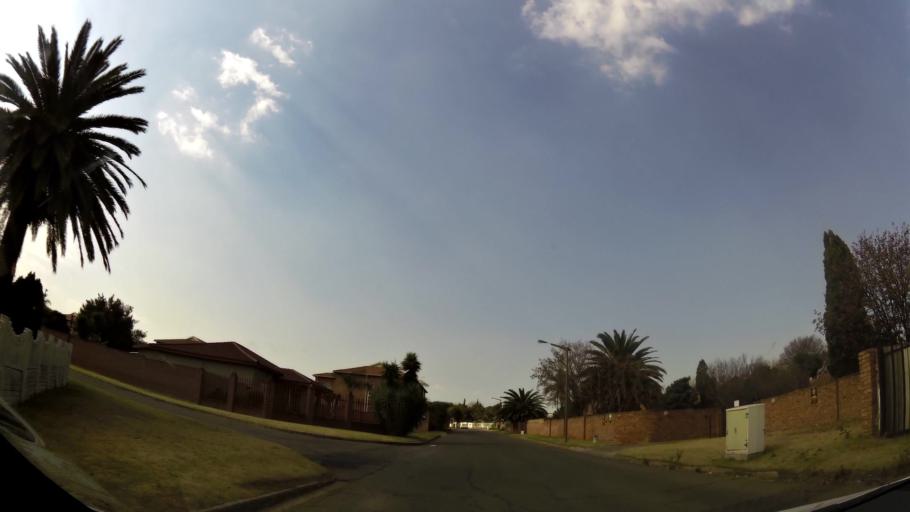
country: ZA
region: Gauteng
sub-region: Ekurhuleni Metropolitan Municipality
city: Germiston
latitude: -26.1834
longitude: 28.2056
